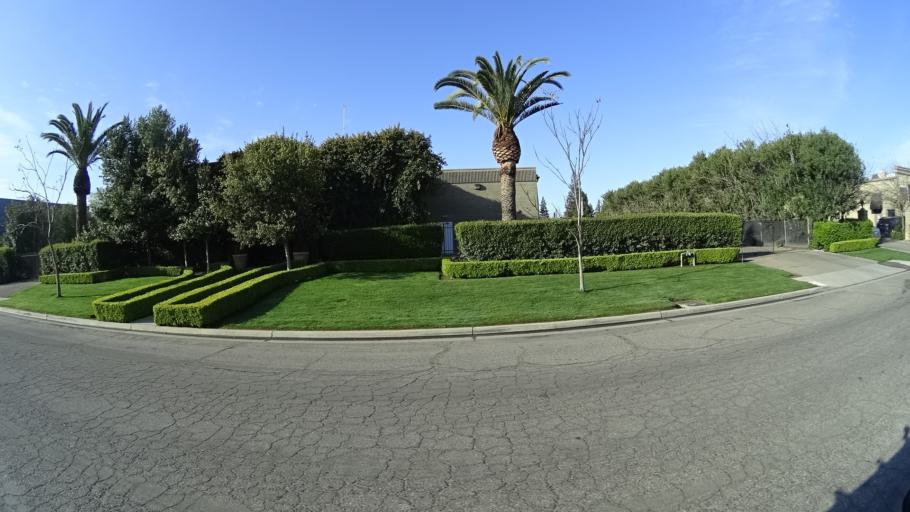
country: US
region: California
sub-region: Fresno County
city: West Park
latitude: 36.8138
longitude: -119.8789
